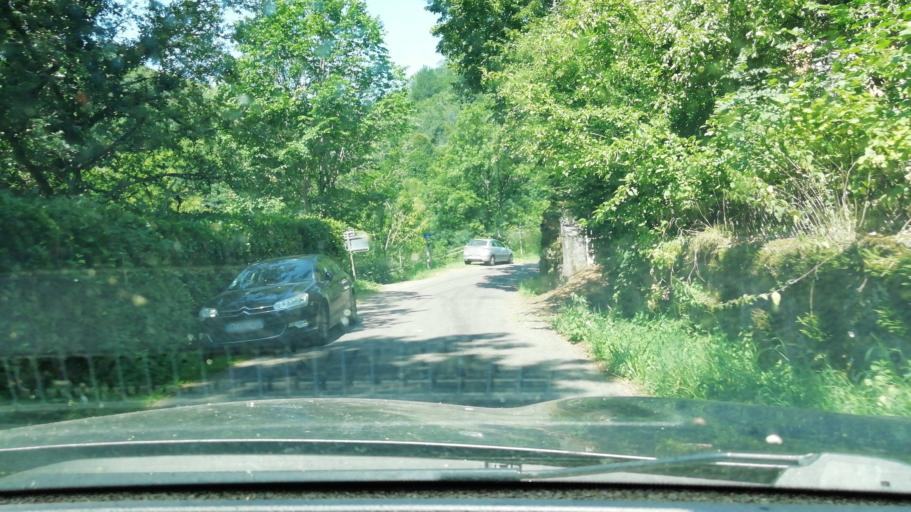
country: FR
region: Auvergne
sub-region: Departement du Cantal
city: Vic-sur-Cere
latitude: 45.0279
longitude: 2.5808
